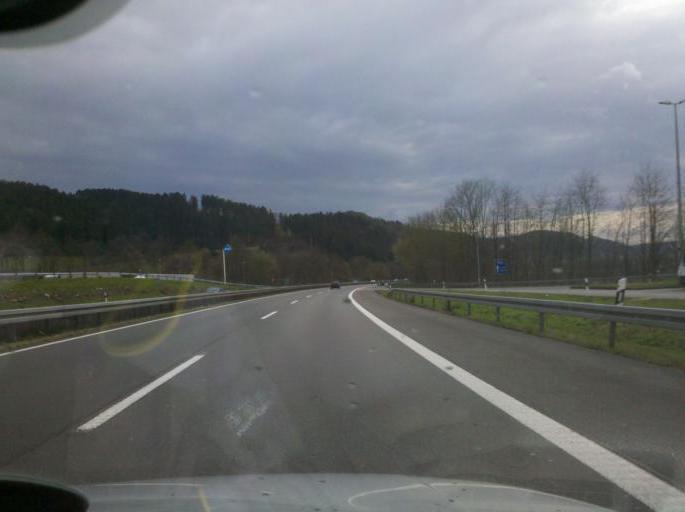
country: DE
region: North Rhine-Westphalia
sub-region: Regierungsbezirk Koln
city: Overath
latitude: 50.9511
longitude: 7.3188
